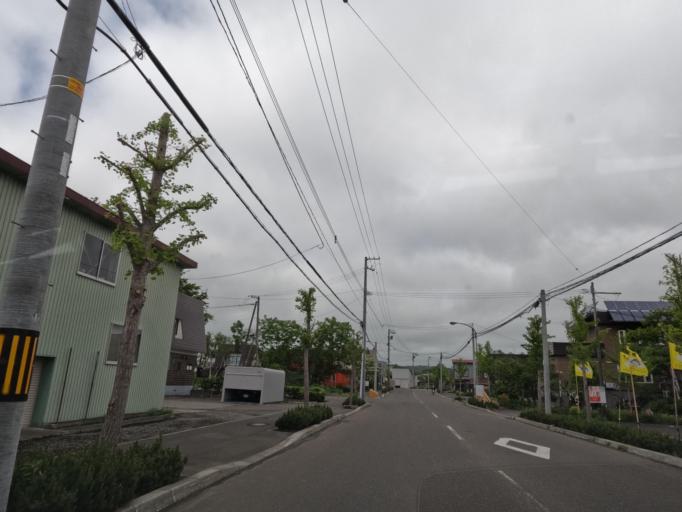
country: JP
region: Hokkaido
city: Tobetsu
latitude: 43.2313
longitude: 141.5160
